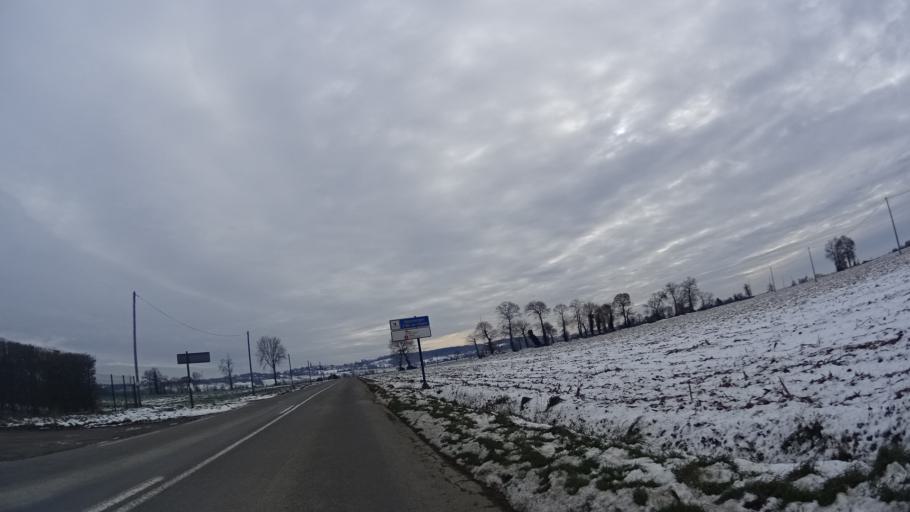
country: FR
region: Brittany
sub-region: Departement des Cotes-d'Armor
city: Plouasne
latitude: 48.3192
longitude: -1.9556
